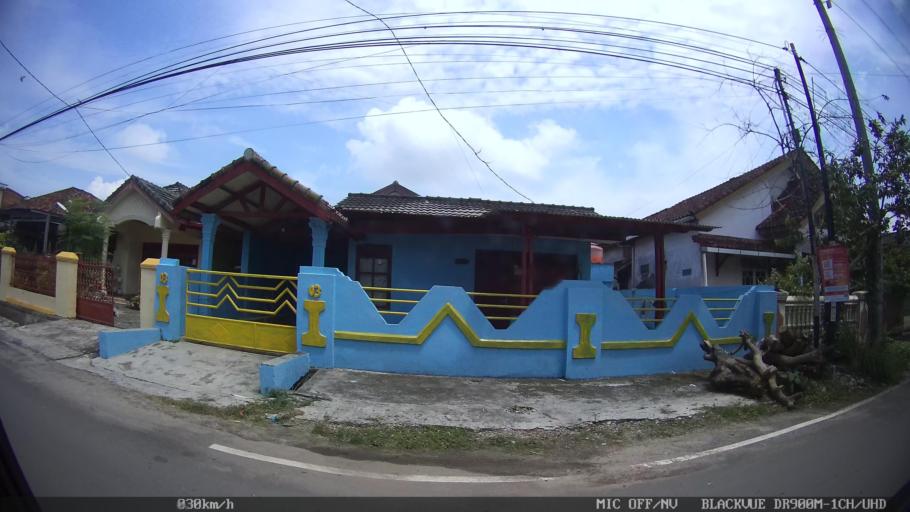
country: ID
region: Lampung
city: Kedaton
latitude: -5.3683
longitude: 105.3032
